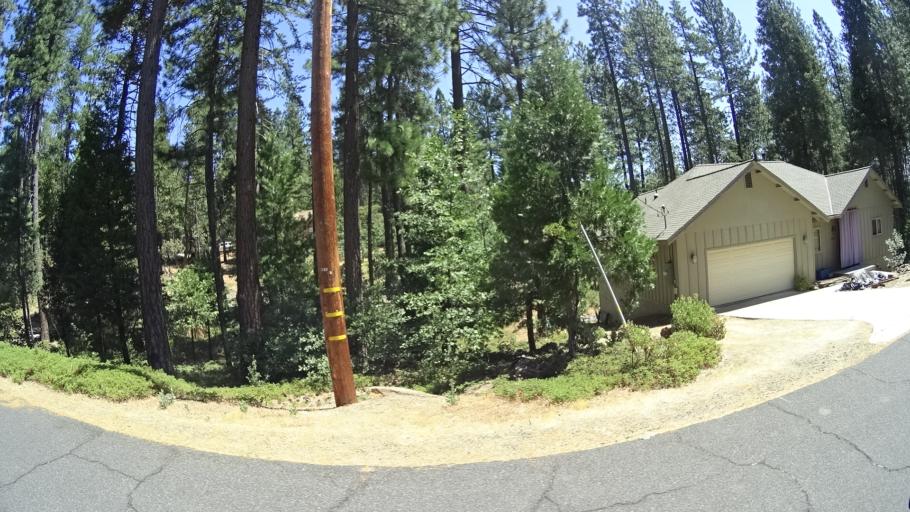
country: US
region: California
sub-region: Calaveras County
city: Forest Meadows
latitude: 38.2068
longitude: -120.3717
